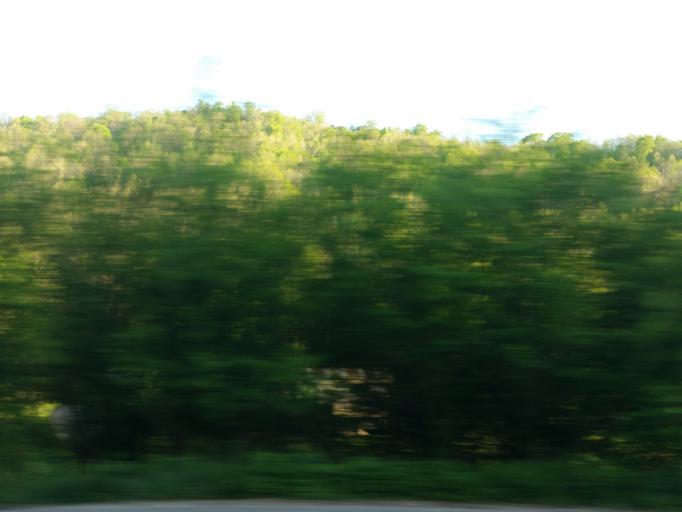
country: US
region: Tennessee
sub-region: Campbell County
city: Jellico
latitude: 36.5516
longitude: -83.9805
